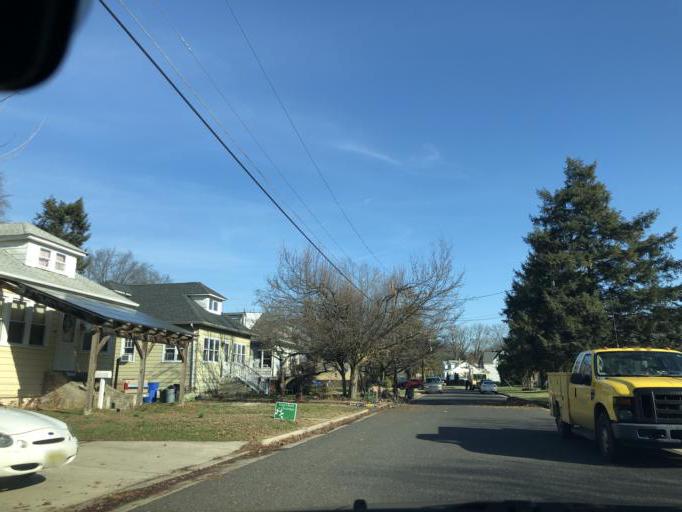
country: US
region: New Jersey
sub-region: Burlington County
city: Maple Shade
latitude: 39.9585
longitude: -74.9833
